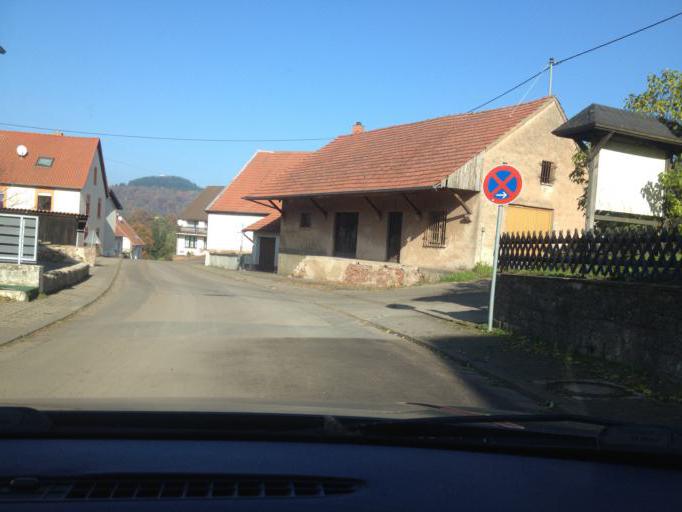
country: DE
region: Saarland
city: Sankt Wendel
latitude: 49.5098
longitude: 7.1912
